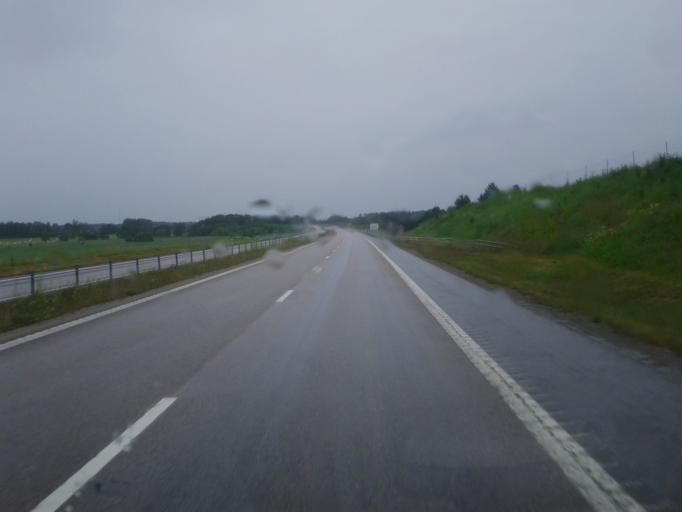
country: SE
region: Uppsala
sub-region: Tierps Kommun
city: Tierp
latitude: 60.3200
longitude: 17.5165
